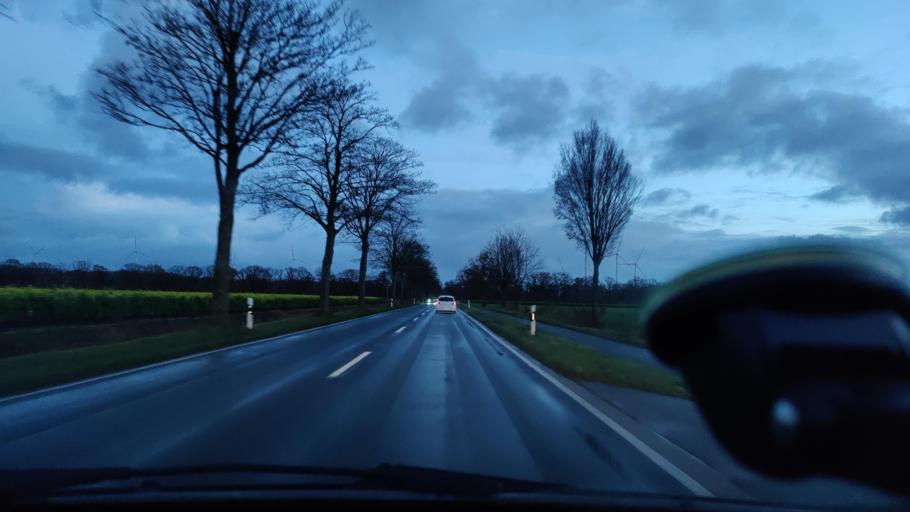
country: NL
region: Limburg
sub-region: Gemeente Bergen
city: Wellerlooi
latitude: 51.5736
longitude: 6.1491
